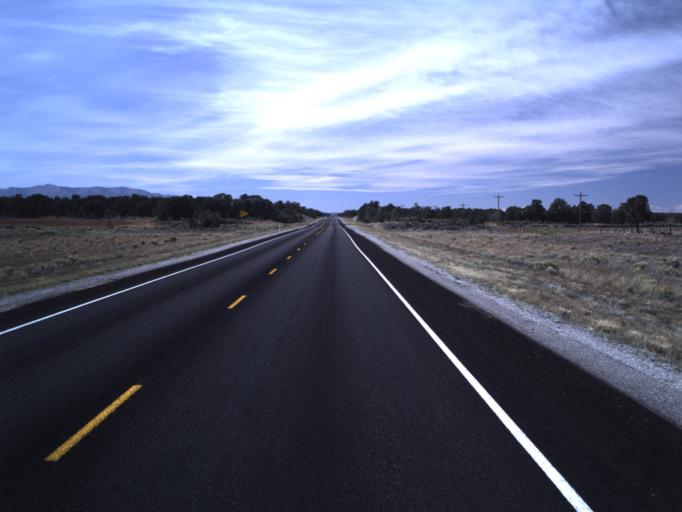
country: US
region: Colorado
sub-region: Dolores County
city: Dove Creek
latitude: 37.8269
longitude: -109.0783
